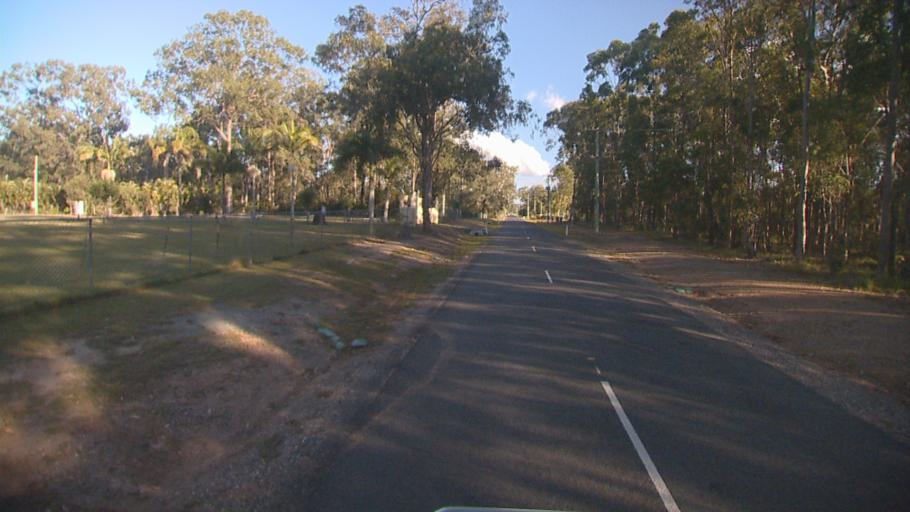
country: AU
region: Queensland
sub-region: Gold Coast
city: Yatala
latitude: -27.6706
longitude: 153.2441
